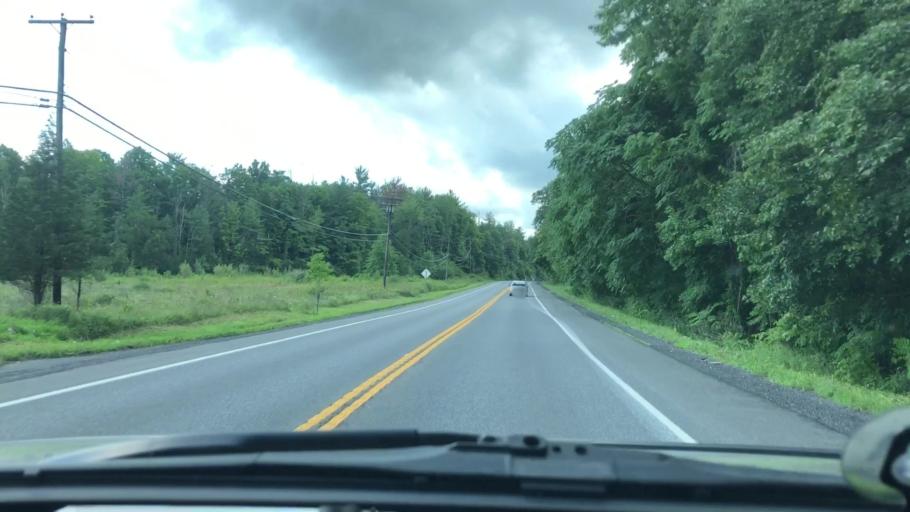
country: US
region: New York
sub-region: Ulster County
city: Saugerties
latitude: 42.1080
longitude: -73.9684
